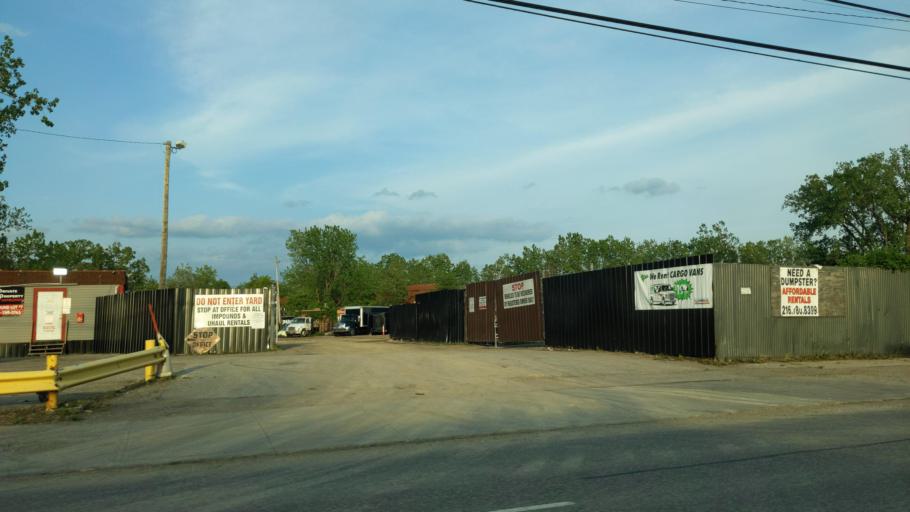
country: US
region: Ohio
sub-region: Cuyahoga County
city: Brook Park
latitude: 41.4356
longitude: -81.7800
